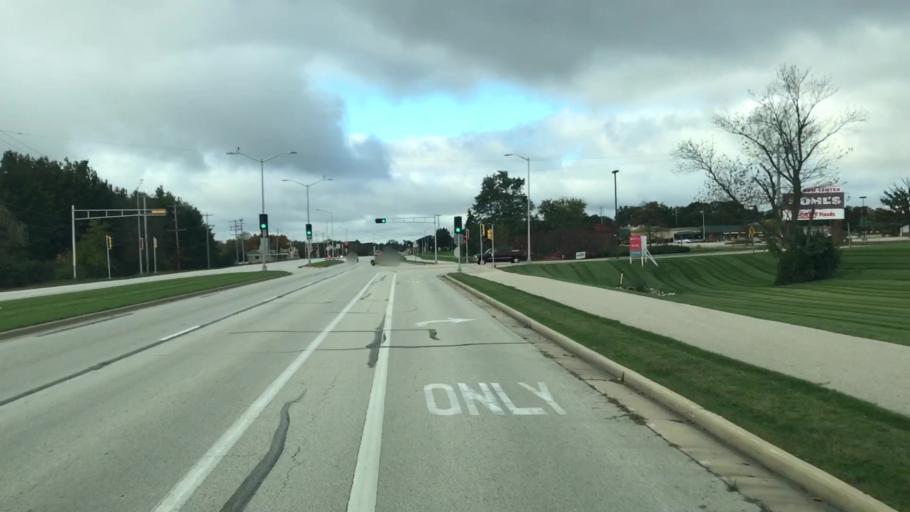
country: US
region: Wisconsin
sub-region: Waukesha County
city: Waukesha
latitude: 42.9911
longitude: -88.2650
